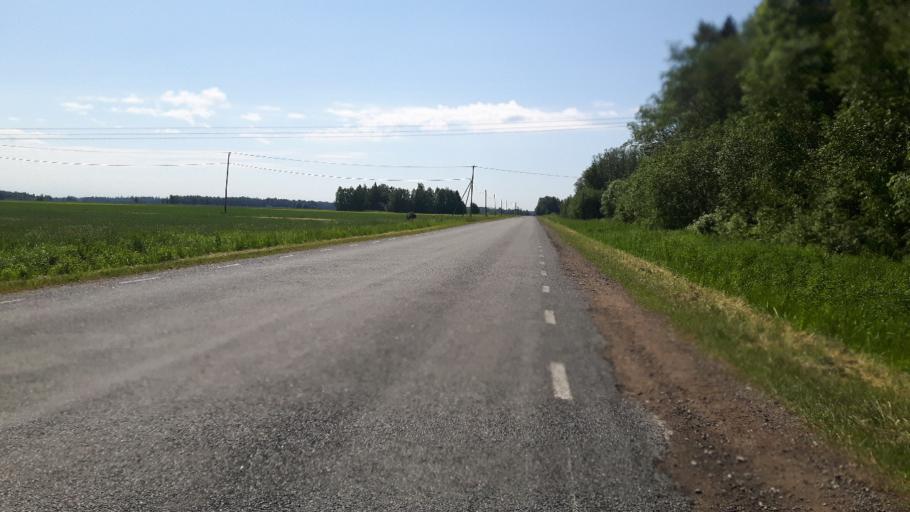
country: EE
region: Paernumaa
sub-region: Vaendra vald (alev)
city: Vandra
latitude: 58.6279
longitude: 25.0209
